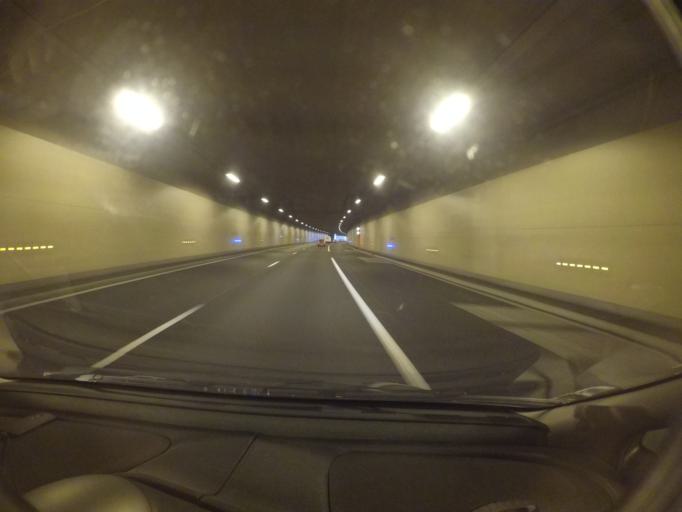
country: FR
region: Pays de la Loire
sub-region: Departement de Maine-et-Loire
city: Avrille
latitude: 47.4903
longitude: -0.5866
